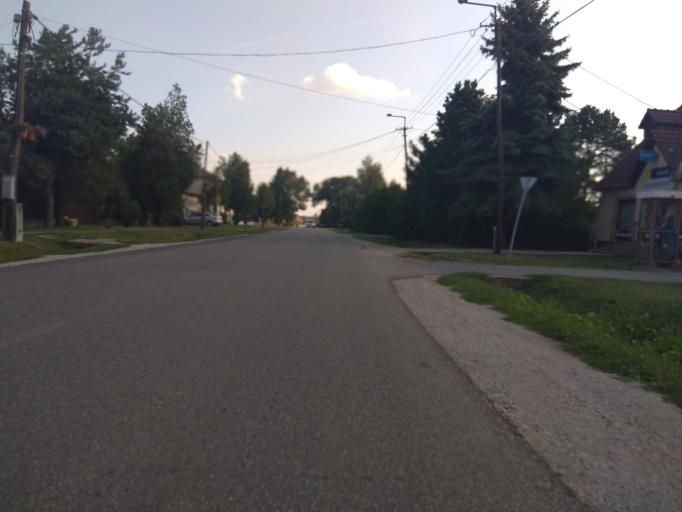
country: HU
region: Borsod-Abauj-Zemplen
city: Mezokeresztes
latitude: 47.8632
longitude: 20.6789
